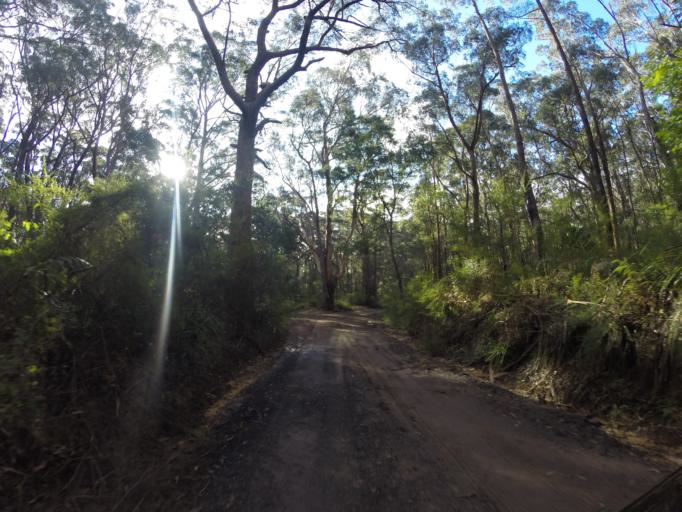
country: AU
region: New South Wales
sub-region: Wollongong
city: Cordeaux Heights
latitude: -34.4167
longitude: 150.7836
